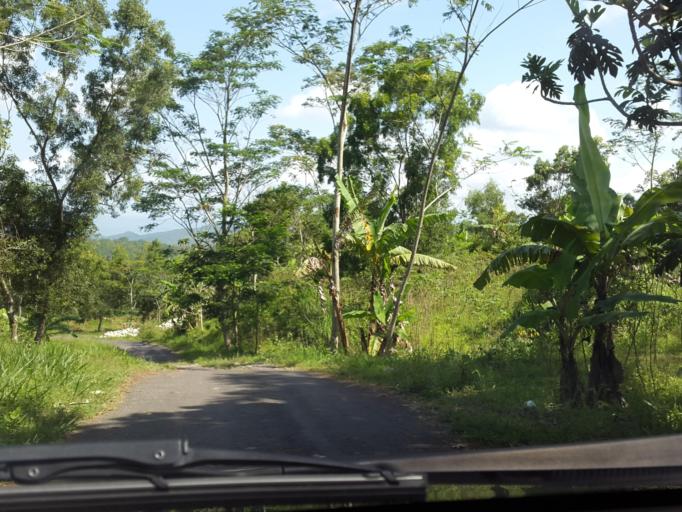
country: ID
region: Central Java
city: Selogiri
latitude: -7.9112
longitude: 110.7683
